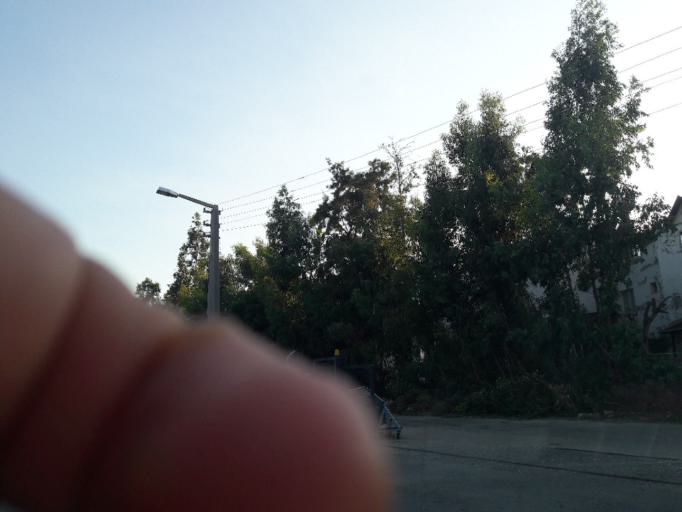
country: TR
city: Yumurtalik
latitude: 36.7747
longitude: 35.7606
